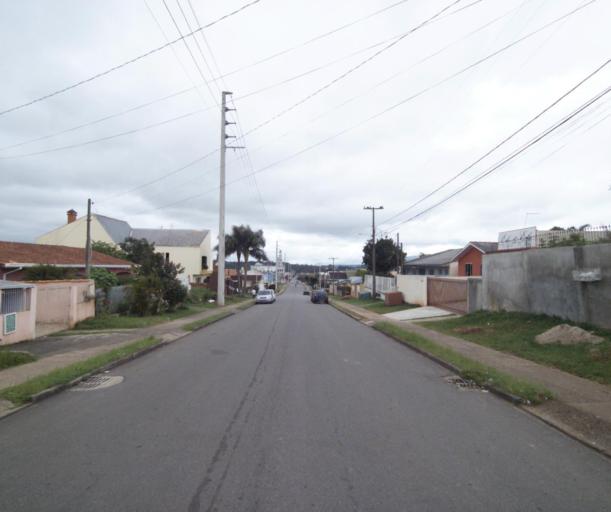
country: BR
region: Parana
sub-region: Quatro Barras
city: Quatro Barras
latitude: -25.3661
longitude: -49.1069
